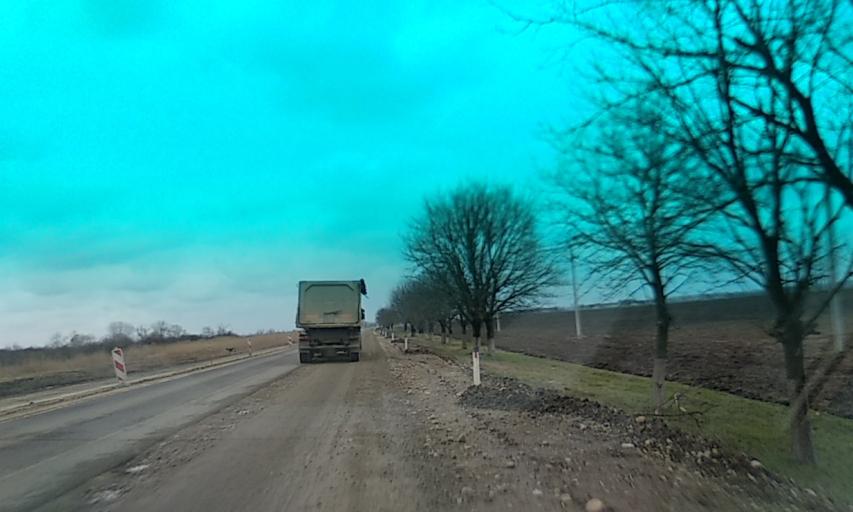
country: RU
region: Krasnodarskiy
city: Velikovechnoye
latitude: 44.9952
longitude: 39.7113
